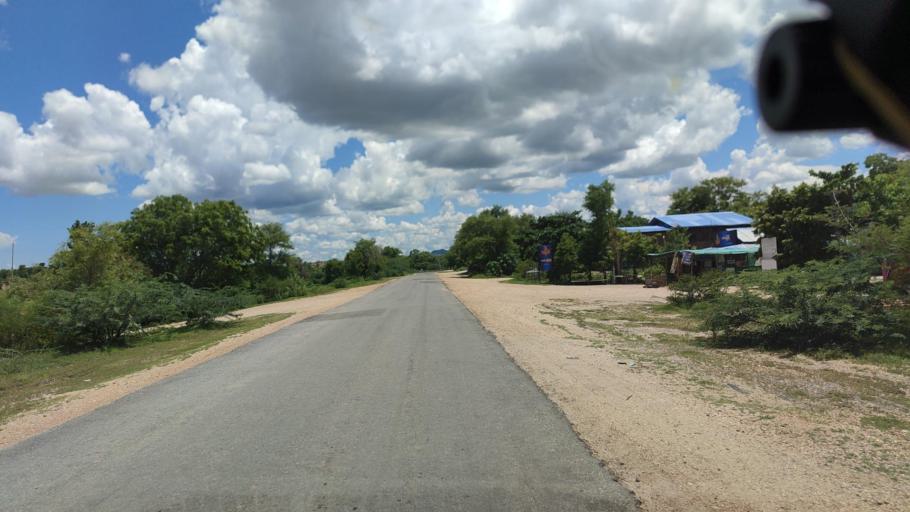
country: MM
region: Magway
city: Magway
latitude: 19.8923
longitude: 95.0799
